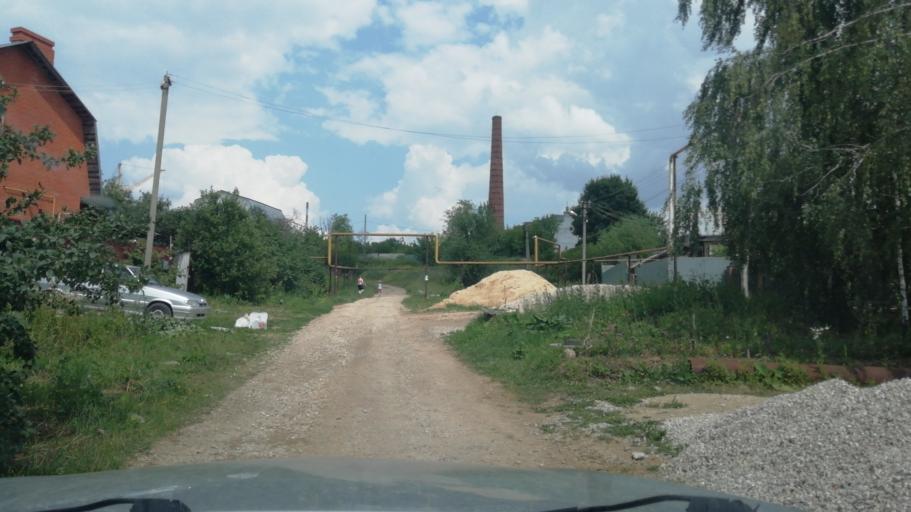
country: RU
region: Tula
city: Mendeleyevskiy
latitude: 54.1603
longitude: 37.5672
